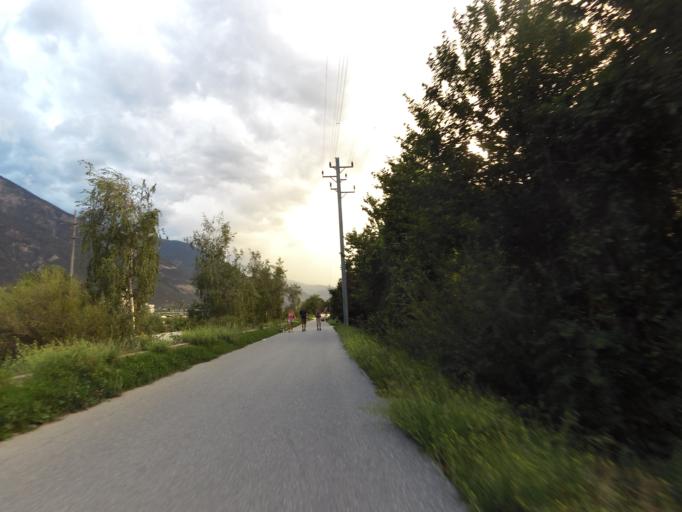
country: CH
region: Valais
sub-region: Brig District
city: Naters
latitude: 46.3221
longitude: 7.9932
